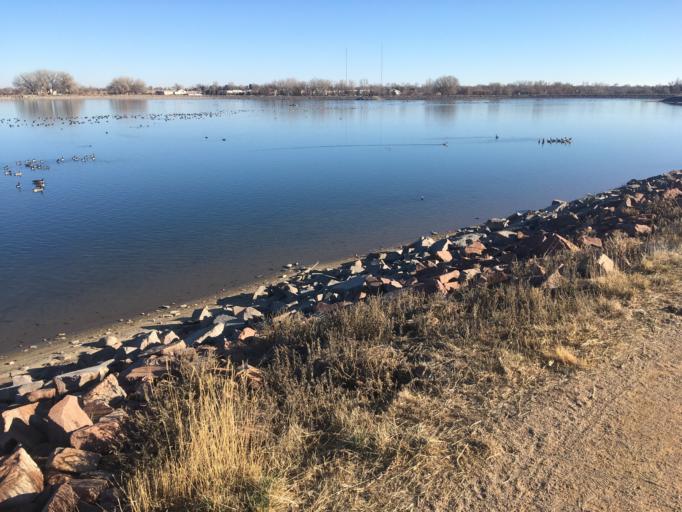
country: US
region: Colorado
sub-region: Weld County
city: Firestone
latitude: 40.1228
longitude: -104.9493
